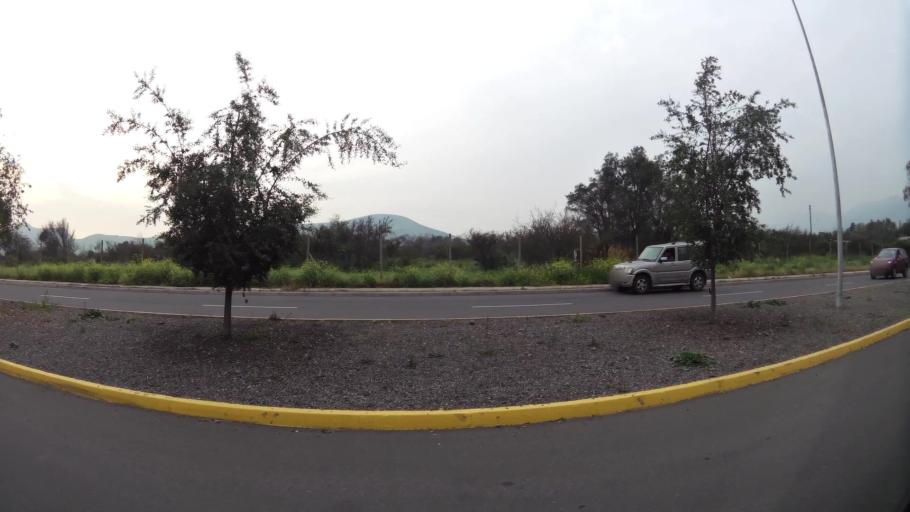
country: CL
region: Santiago Metropolitan
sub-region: Provincia de Chacabuco
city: Chicureo Abajo
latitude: -33.2647
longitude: -70.6226
